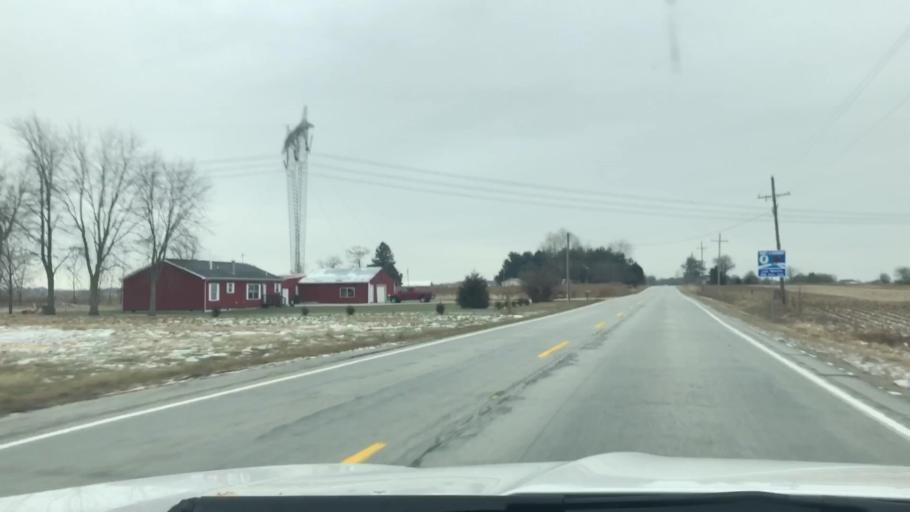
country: US
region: Indiana
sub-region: Fulton County
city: Rochester
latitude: 41.0544
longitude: -86.1443
